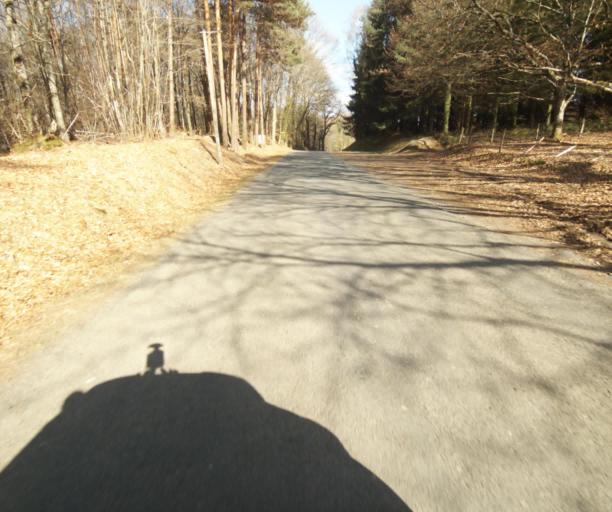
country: FR
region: Limousin
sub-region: Departement de la Correze
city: Saint-Mexant
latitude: 45.3334
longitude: 1.6185
